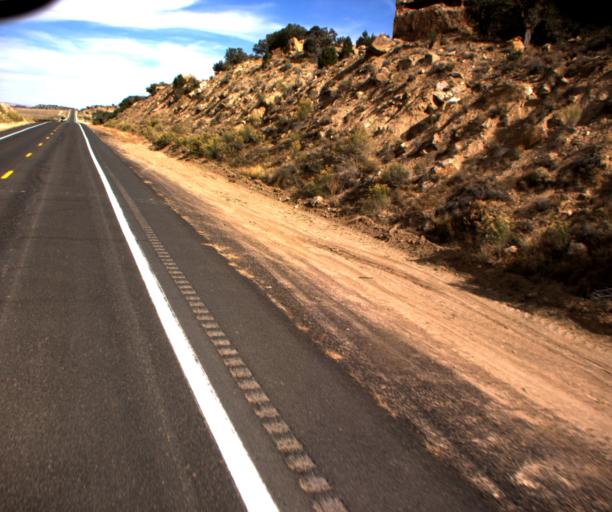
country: US
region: Arizona
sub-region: Navajo County
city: Kayenta
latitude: 36.6656
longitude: -110.4120
